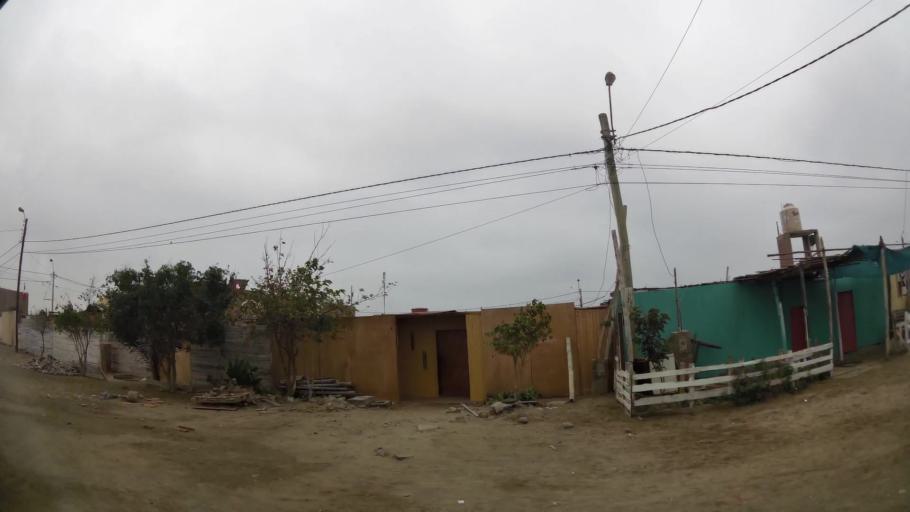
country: PE
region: Ica
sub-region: Provincia de Pisco
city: Paracas
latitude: -13.8357
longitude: -76.2470
